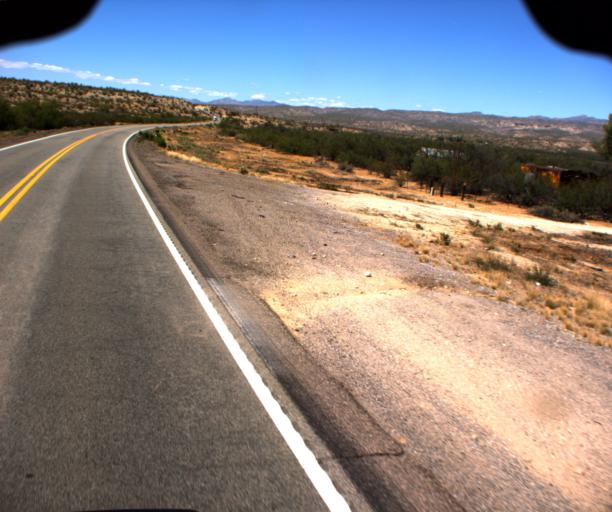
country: US
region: Arizona
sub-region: Yavapai County
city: Bagdad
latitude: 34.7875
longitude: -113.6240
